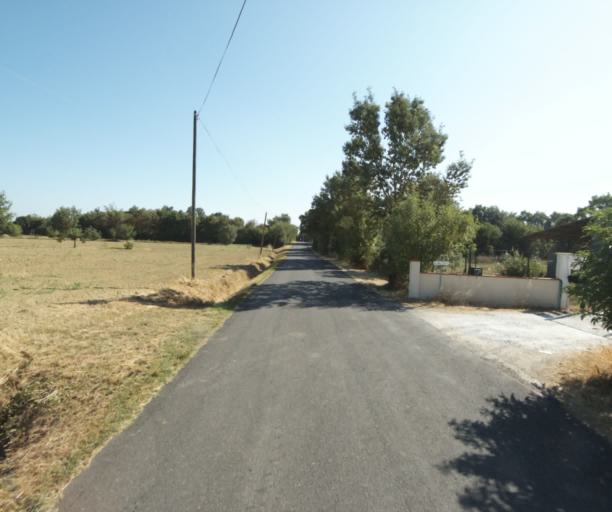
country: FR
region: Midi-Pyrenees
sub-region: Departement de la Haute-Garonne
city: Revel
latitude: 43.4759
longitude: 1.9998
